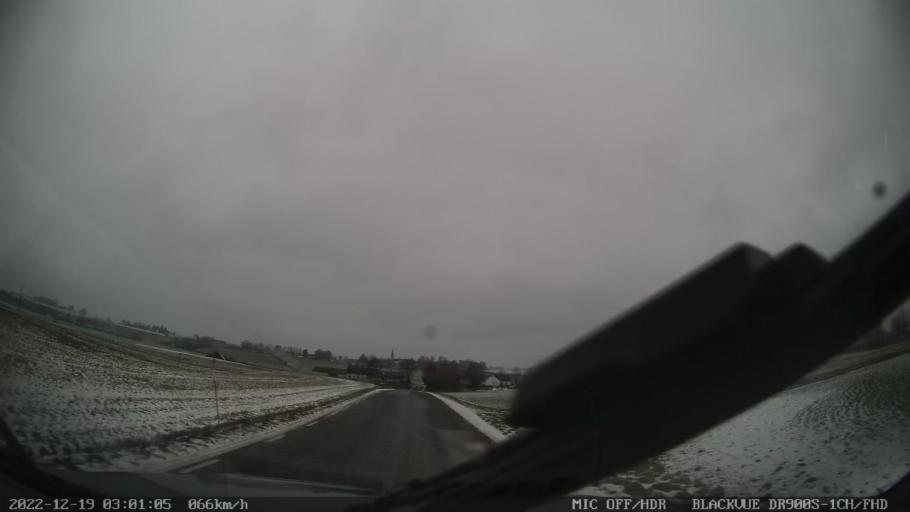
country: SE
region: Skane
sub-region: Tomelilla Kommun
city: Tomelilla
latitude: 55.5197
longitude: 14.0435
